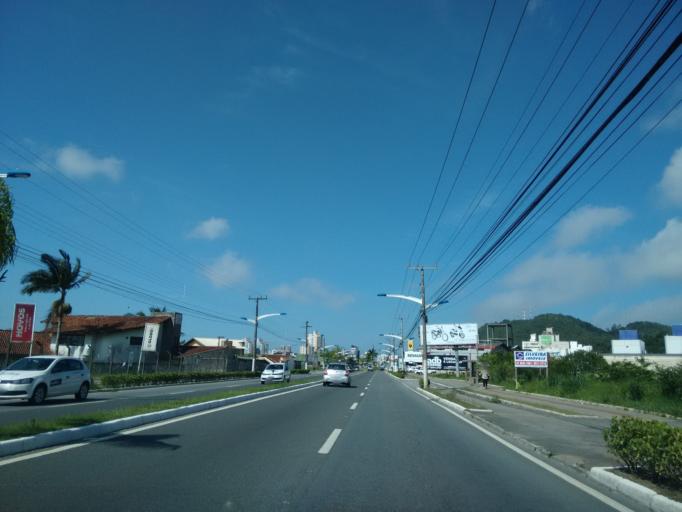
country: BR
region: Santa Catarina
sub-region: Itajai
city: Itajai
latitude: -26.9259
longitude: -48.6795
